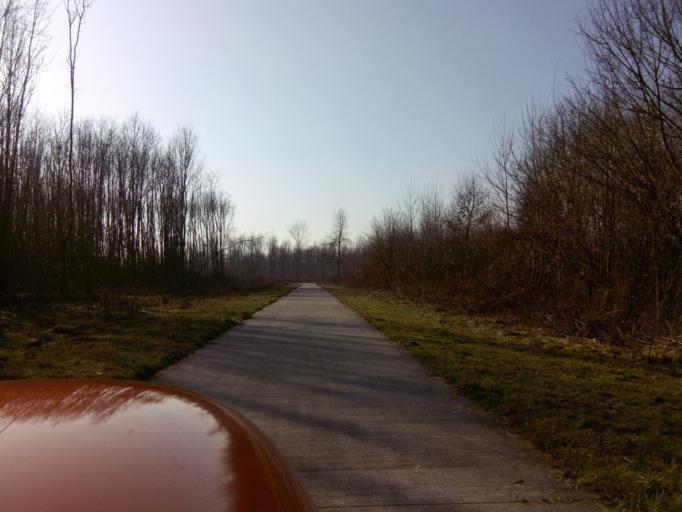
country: NL
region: Gelderland
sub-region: Gemeente Nijkerk
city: Nijkerk
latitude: 52.2890
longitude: 5.4856
